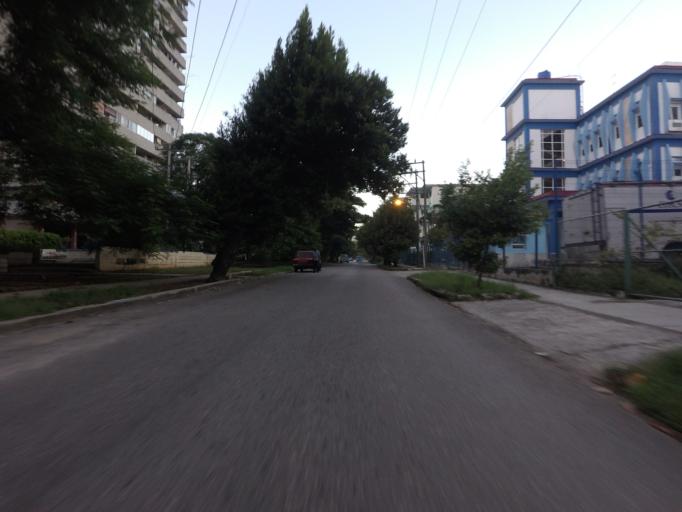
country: CU
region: La Habana
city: Havana
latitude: 23.1192
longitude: -82.3926
